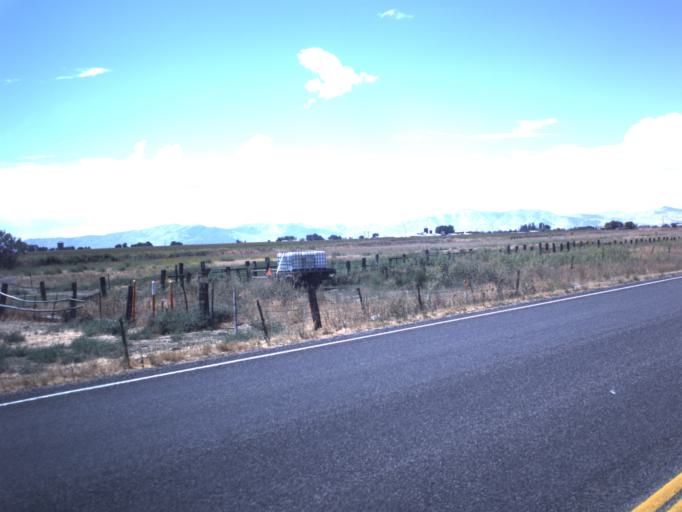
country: US
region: Utah
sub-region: Box Elder County
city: Honeyville
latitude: 41.5596
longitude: -112.1500
